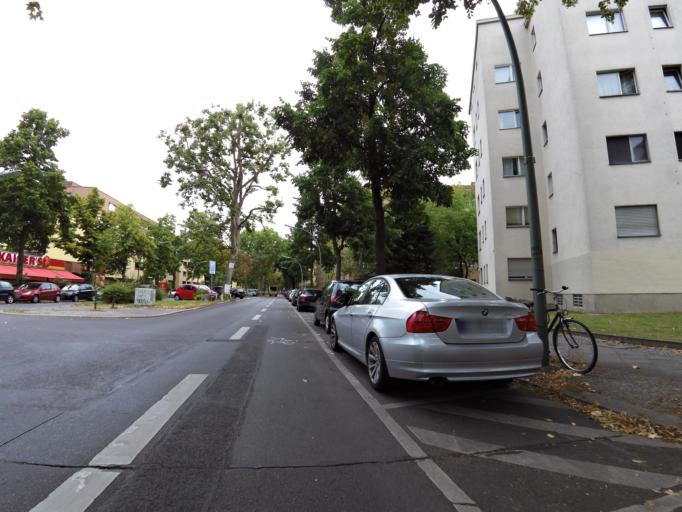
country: DE
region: Berlin
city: Wilmersdorf Bezirk
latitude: 52.4682
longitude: 13.3116
